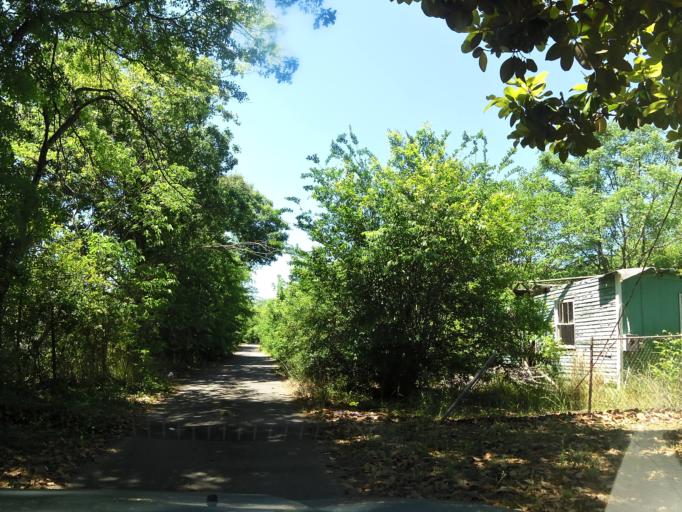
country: US
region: Georgia
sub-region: Richmond County
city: Augusta
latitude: 33.4571
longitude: -81.9760
